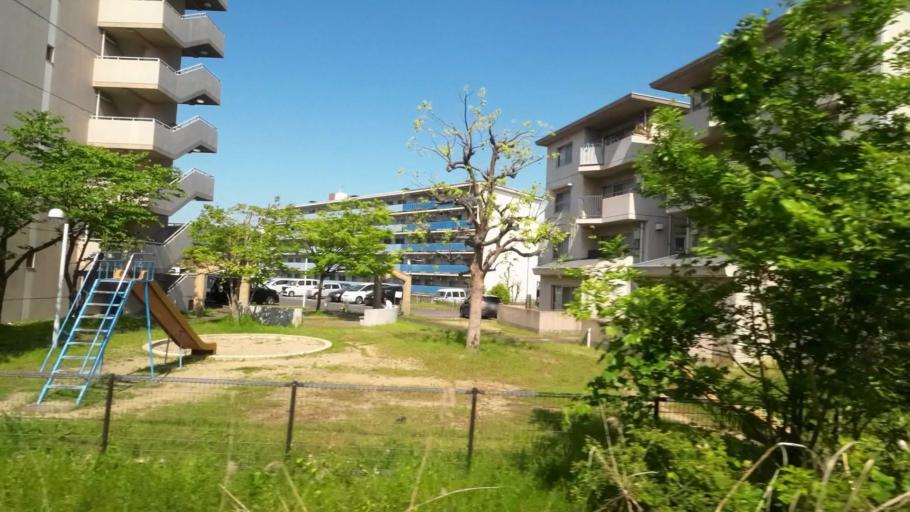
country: JP
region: Kagawa
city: Tadotsu
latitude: 34.2664
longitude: 133.7544
